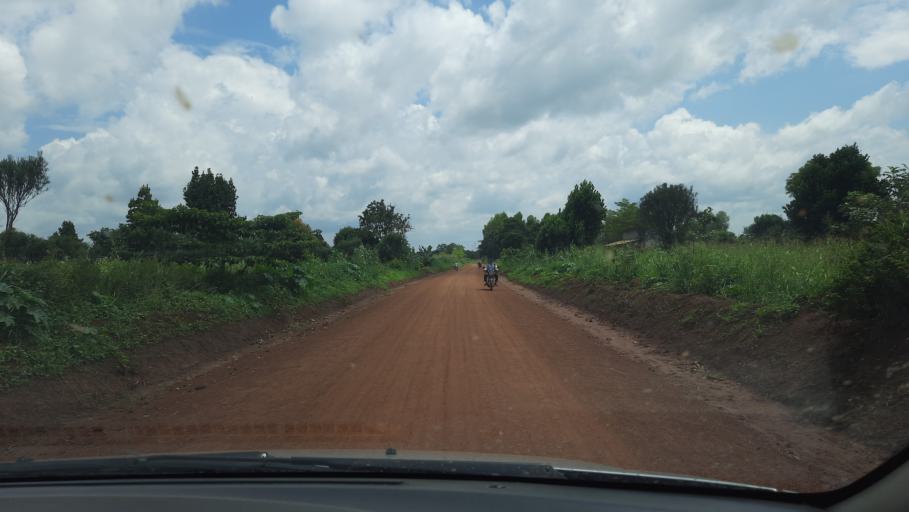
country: UG
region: Western Region
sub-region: Kiryandongo District
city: Kiryandongo
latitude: 1.8177
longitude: 31.9888
